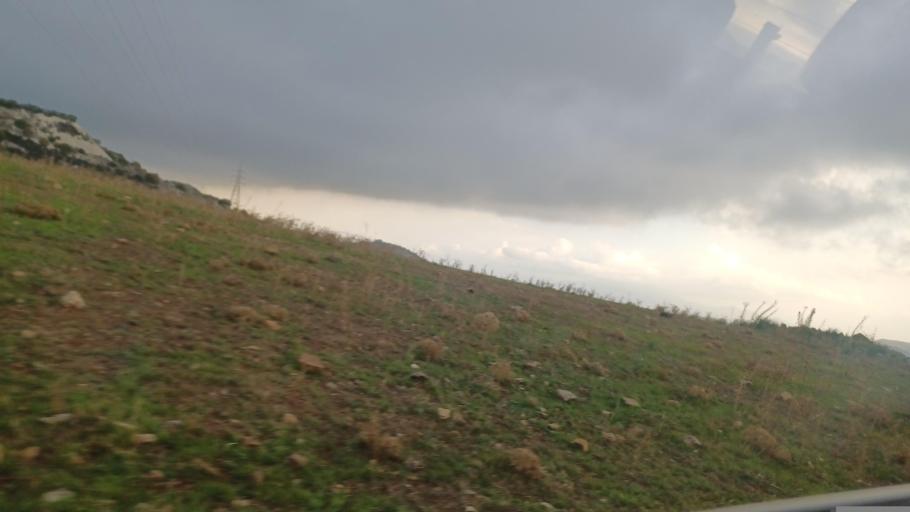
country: CY
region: Pafos
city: Mesogi
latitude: 34.7848
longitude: 32.5119
